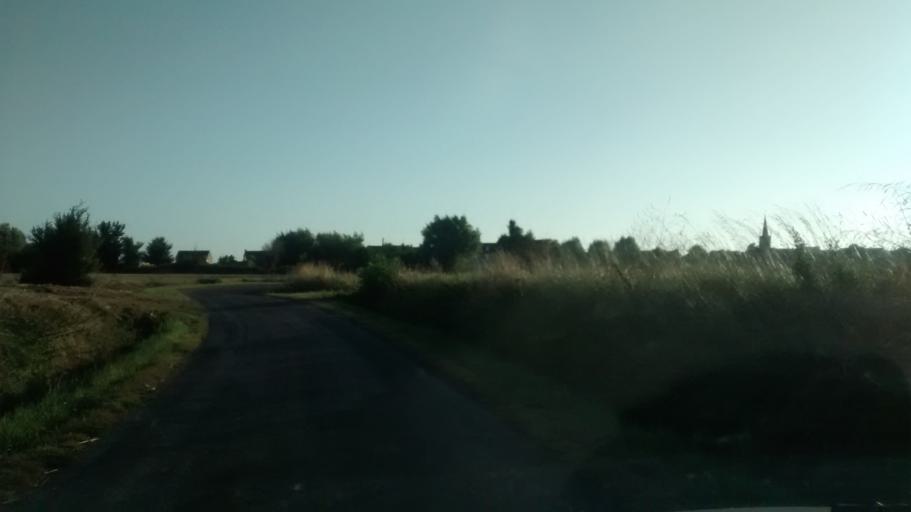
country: FR
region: Brittany
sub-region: Departement d'Ille-et-Vilaine
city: La Fresnais
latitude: 48.6113
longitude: -1.8472
